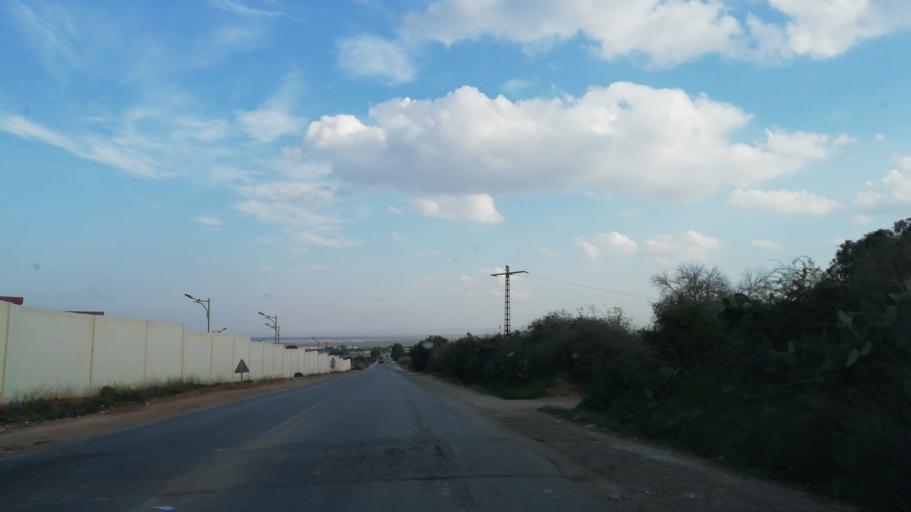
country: DZ
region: Relizane
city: Relizane
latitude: 35.9048
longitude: 0.5152
